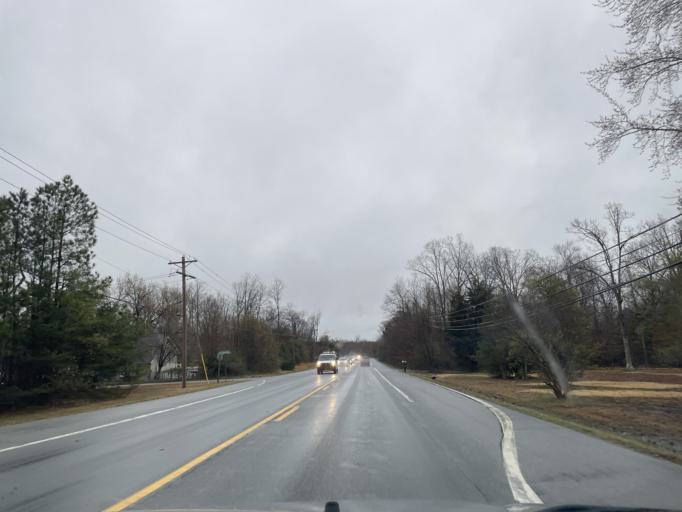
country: US
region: Maryland
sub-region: Charles County
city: La Plata
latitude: 38.5279
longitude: -76.9559
